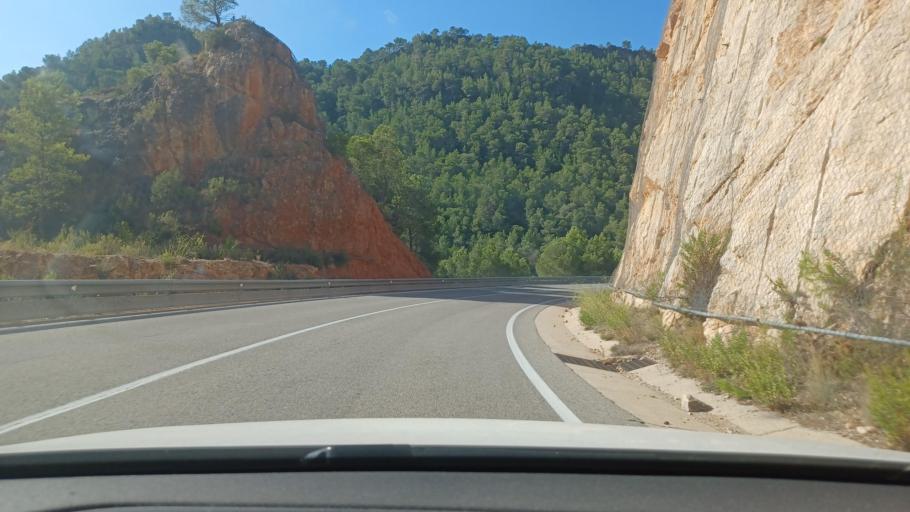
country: ES
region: Catalonia
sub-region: Provincia de Tarragona
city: Bot
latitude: 40.9714
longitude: 0.4327
